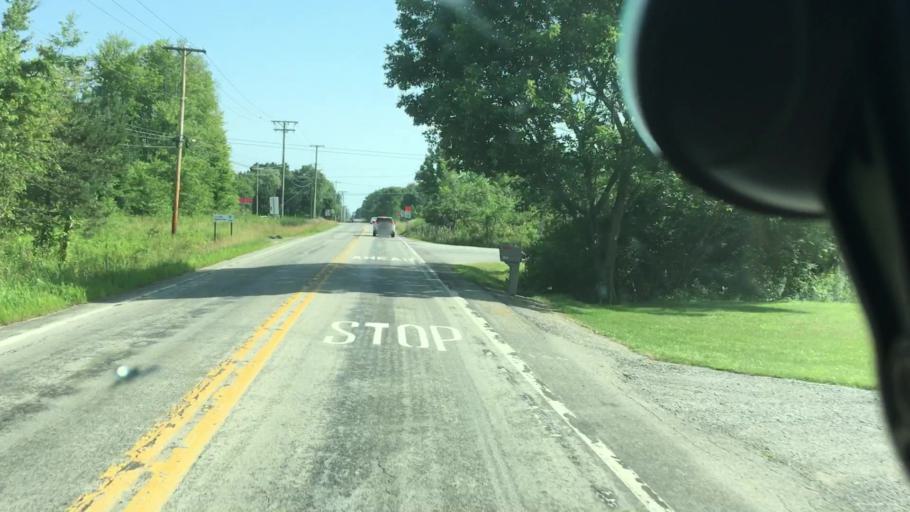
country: US
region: Pennsylvania
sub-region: Lawrence County
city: New Castle
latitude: 41.0110
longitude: -80.2695
